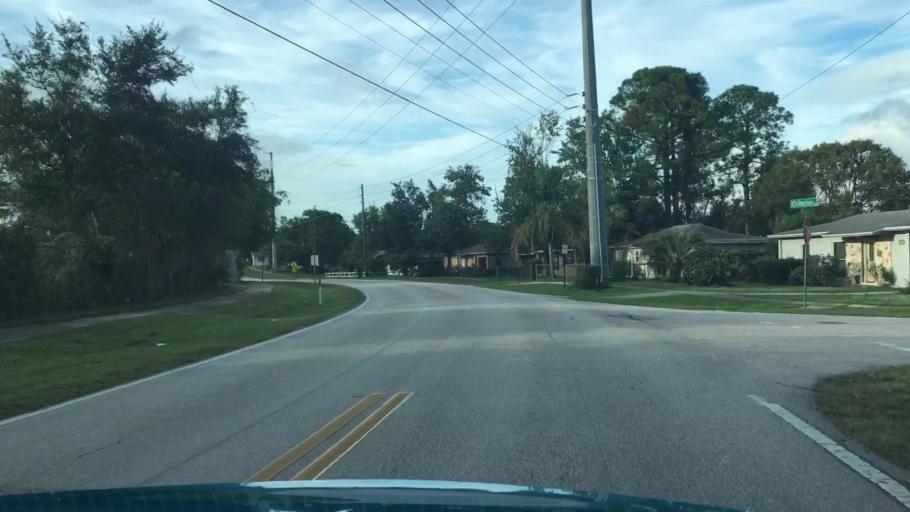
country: US
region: Florida
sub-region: Volusia County
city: Deltona
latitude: 28.8949
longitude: -81.2331
